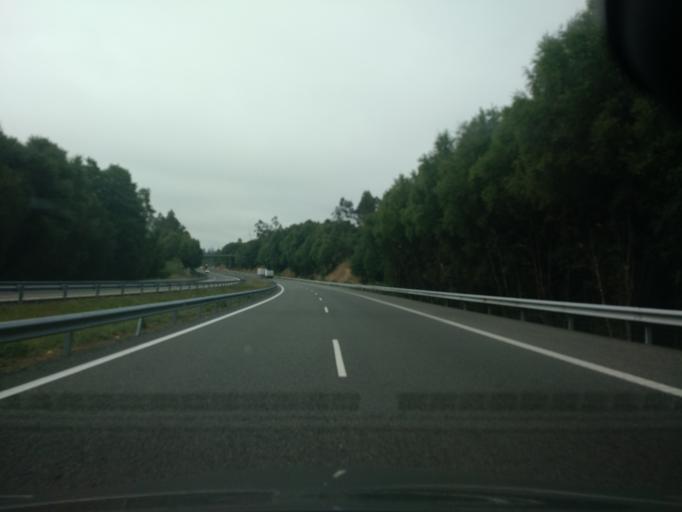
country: ES
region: Galicia
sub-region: Provincia da Coruna
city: Mesia
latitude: 43.1327
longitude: -8.3309
